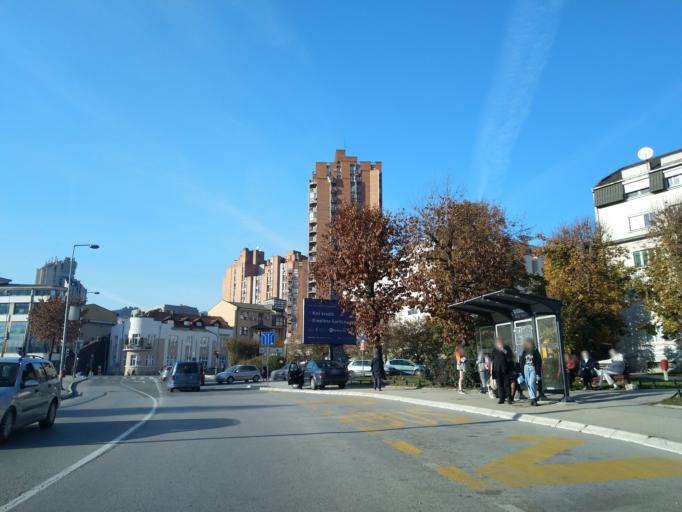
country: RS
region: Central Serbia
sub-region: Zlatiborski Okrug
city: Uzice
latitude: 43.8542
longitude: 19.8431
